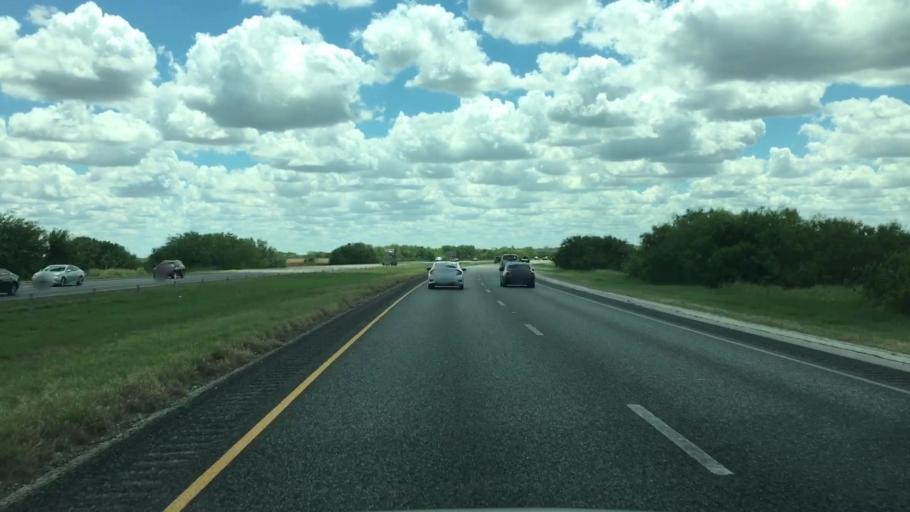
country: US
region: Texas
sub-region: Bexar County
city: Elmendorf
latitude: 29.3004
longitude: -98.3955
